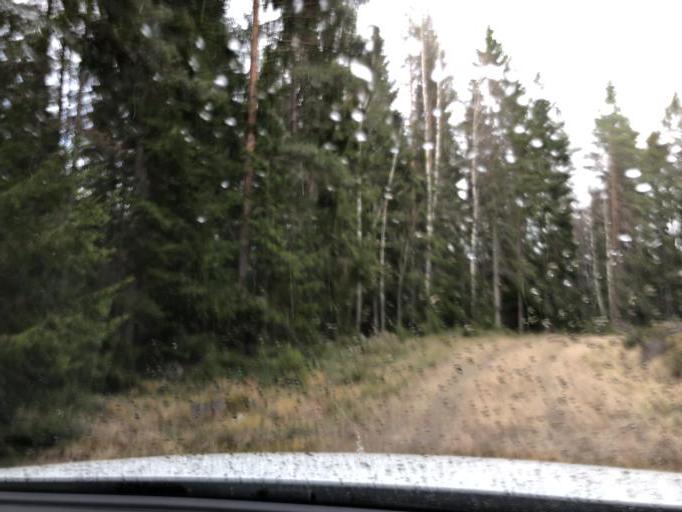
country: SE
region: Gaevleborg
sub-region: Gavle Kommun
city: Hedesunda
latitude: 60.3400
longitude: 17.0837
